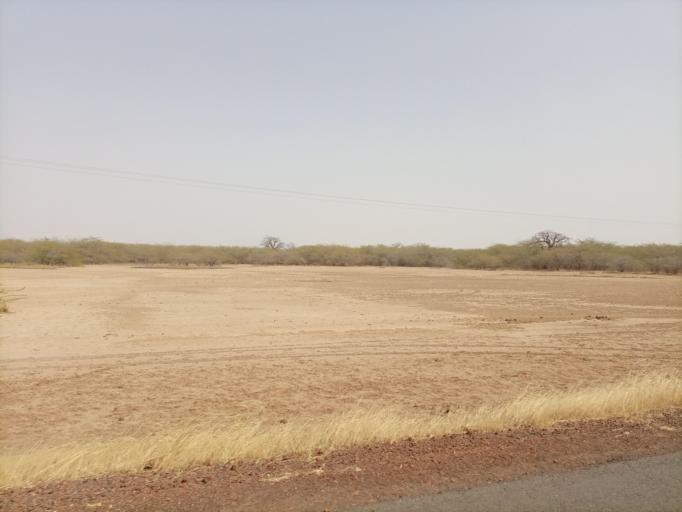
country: SN
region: Fatick
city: Foundiougne
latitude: 14.1785
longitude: -16.4578
